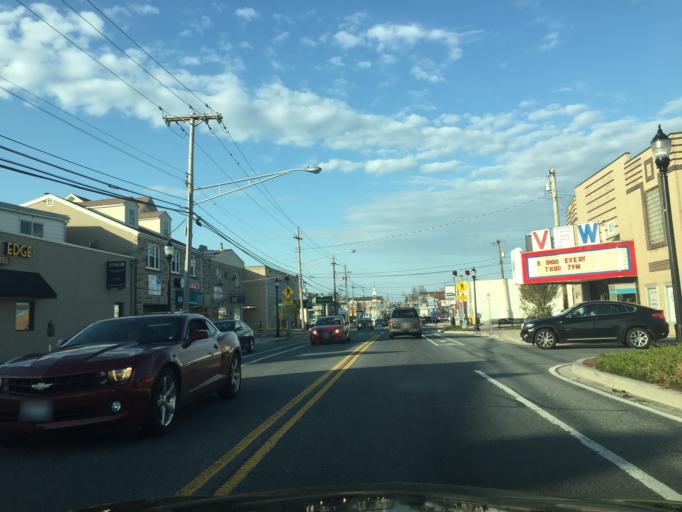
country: US
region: Maryland
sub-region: Baltimore County
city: Parkville
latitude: 39.3776
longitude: -76.5395
